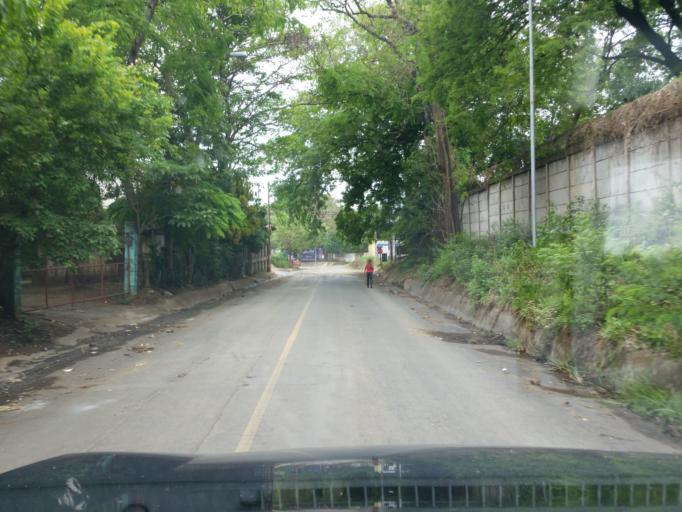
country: NI
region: Managua
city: Managua
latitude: 12.0872
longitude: -86.2423
